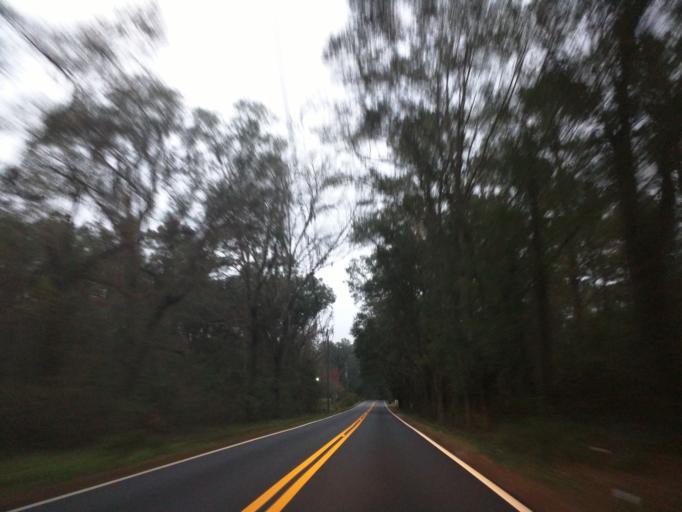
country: US
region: Florida
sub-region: Gadsden County
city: Havana
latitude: 30.5713
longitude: -84.3603
